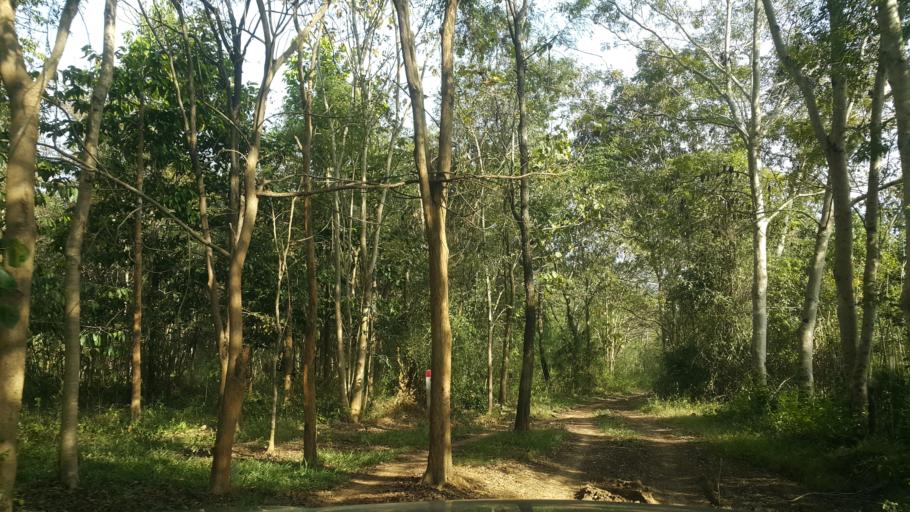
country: TH
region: Chiang Mai
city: Mae On
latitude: 18.7468
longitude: 99.2065
